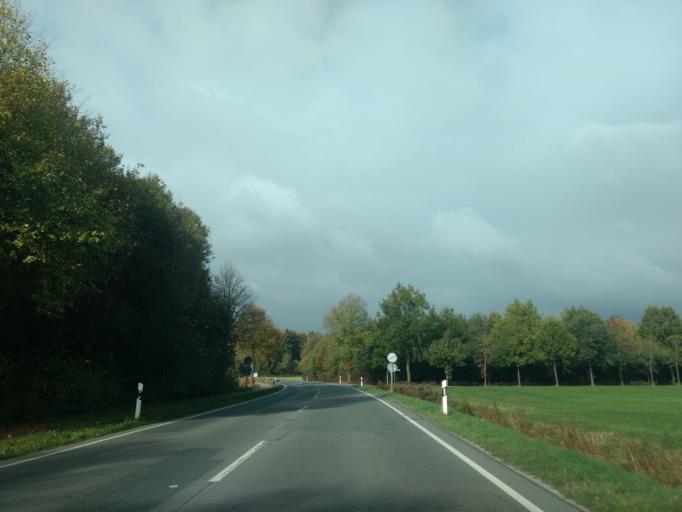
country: DE
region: Lower Saxony
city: Bad Laer
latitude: 52.1433
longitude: 8.0917
